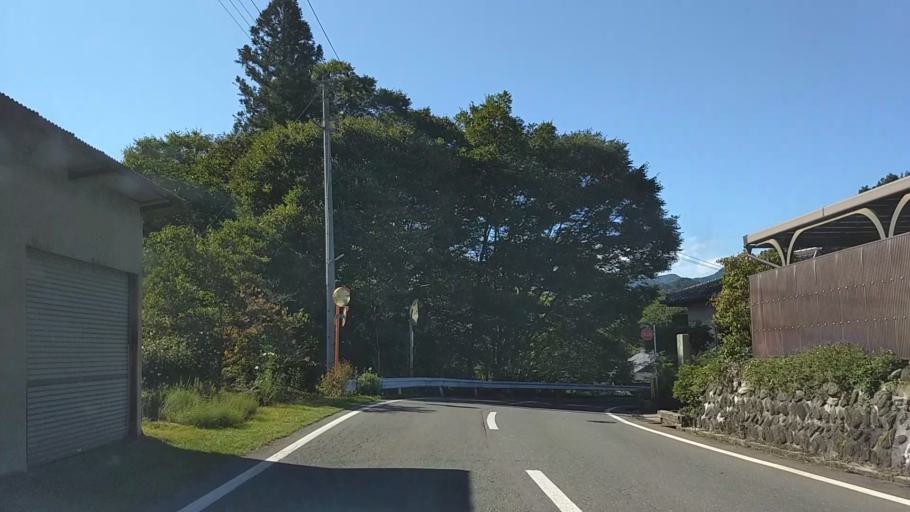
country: JP
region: Nagano
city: Nagano-shi
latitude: 36.6055
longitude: 138.0930
